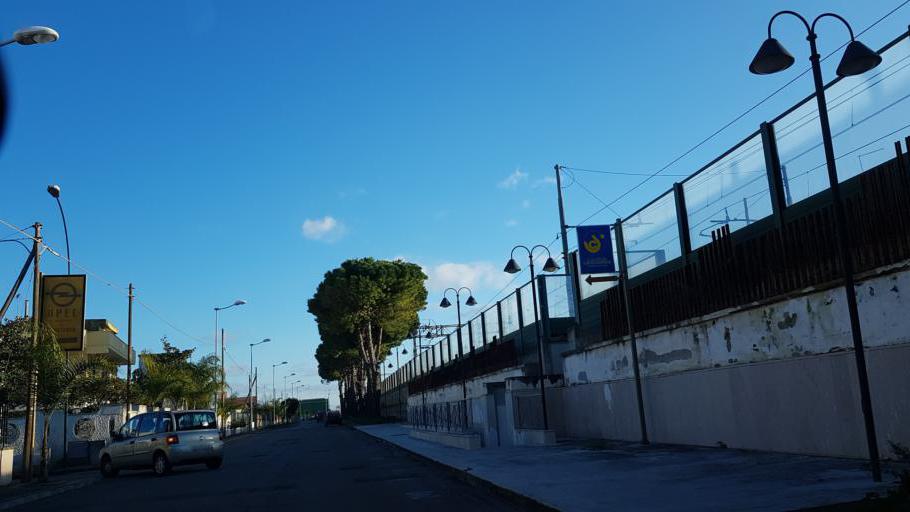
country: IT
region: Apulia
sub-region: Provincia di Lecce
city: Squinzano
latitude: 40.4356
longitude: 18.0503
